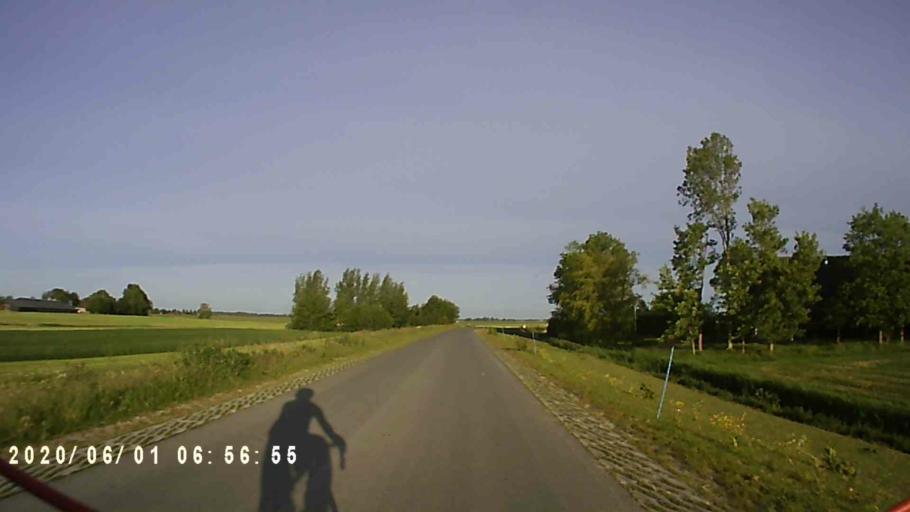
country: NL
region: Friesland
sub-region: Gemeente Kollumerland en Nieuwkruisland
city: Kollum
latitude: 53.3165
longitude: 6.1091
